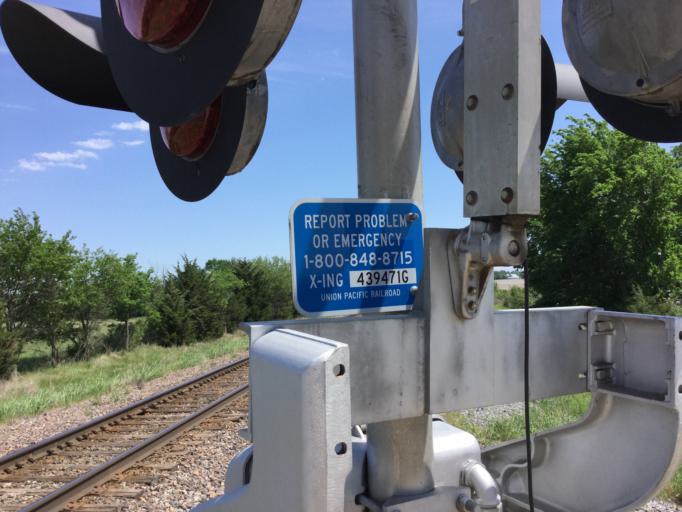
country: US
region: Kansas
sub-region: Coffey County
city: Burlington
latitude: 38.1401
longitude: -95.5632
